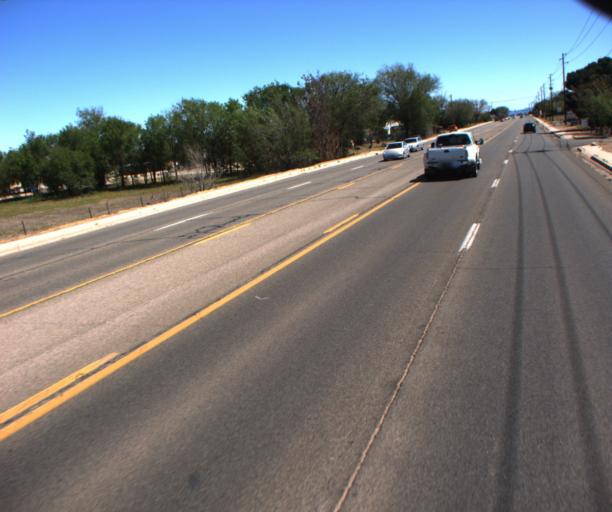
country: US
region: Arizona
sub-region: Yavapai County
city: Chino Valley
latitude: 34.7507
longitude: -112.4543
